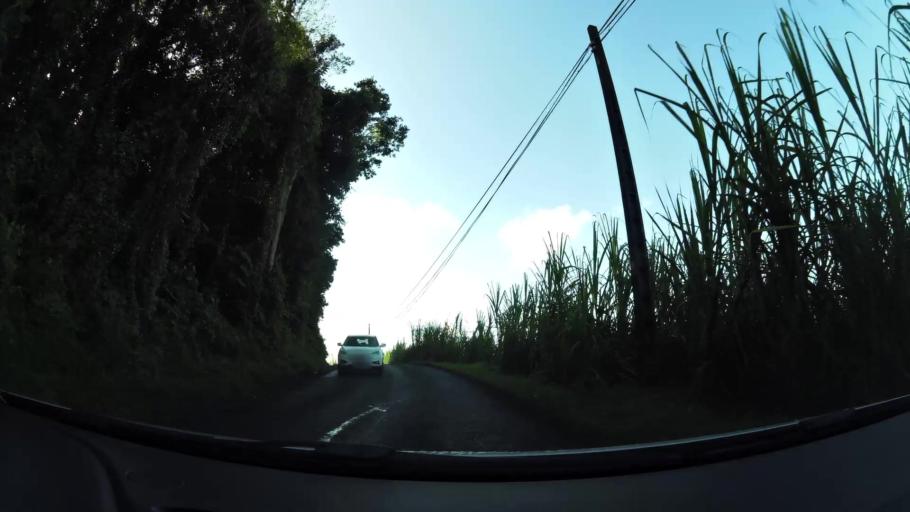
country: MQ
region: Martinique
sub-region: Martinique
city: Le Lamentin
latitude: 14.6327
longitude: -61.0320
